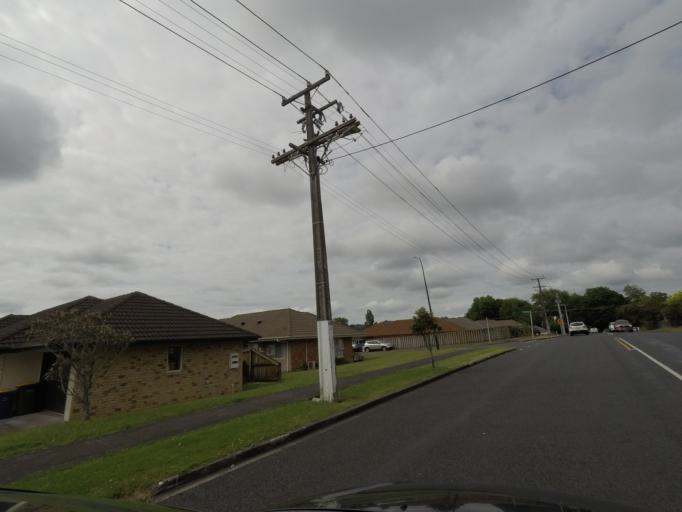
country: NZ
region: Auckland
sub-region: Auckland
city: Waitakere
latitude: -36.9022
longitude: 174.6216
